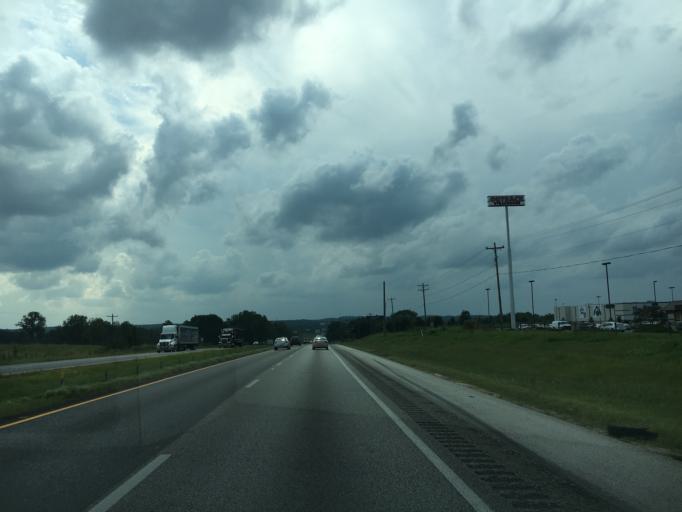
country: US
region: South Carolina
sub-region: Cherokee County
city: Gaffney
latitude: 35.0807
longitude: -81.7117
